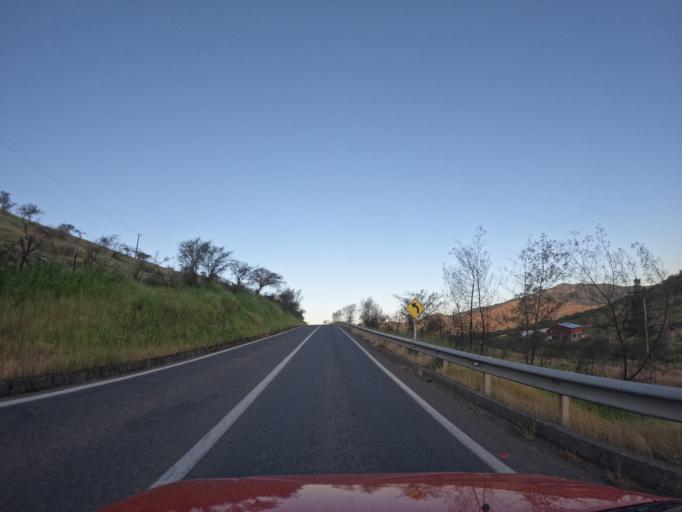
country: CL
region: Maule
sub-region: Provincia de Curico
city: Rauco
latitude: -35.0773
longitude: -71.6291
